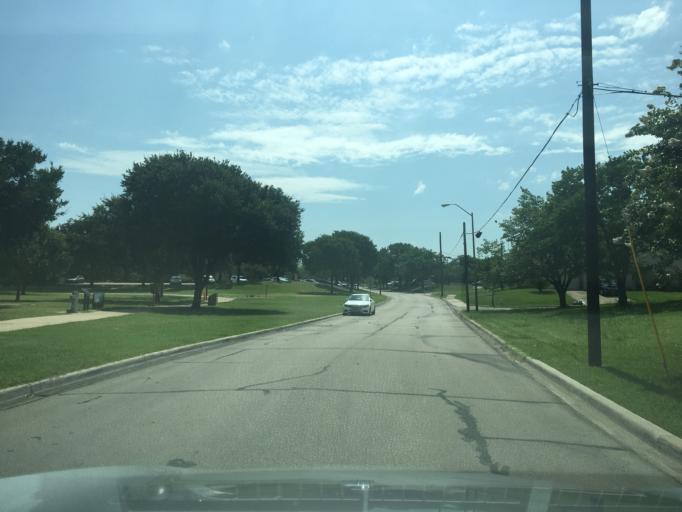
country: US
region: Texas
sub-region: Dallas County
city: Farmers Branch
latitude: 32.9322
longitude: -96.8764
